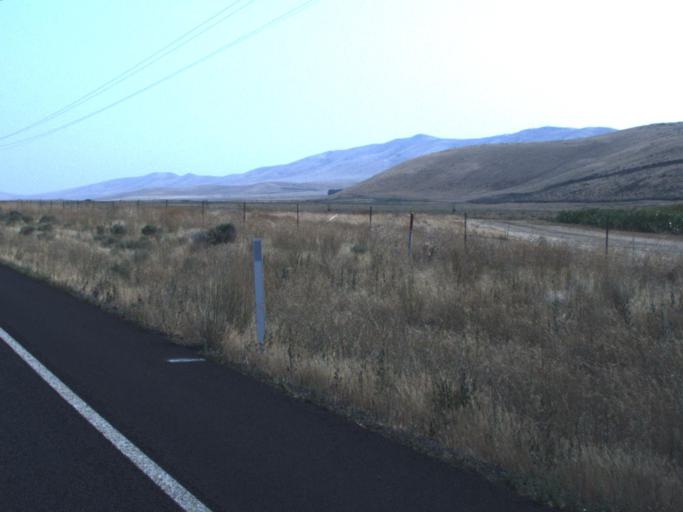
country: US
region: Washington
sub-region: Yakima County
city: Sunnyside
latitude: 46.5077
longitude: -120.0785
